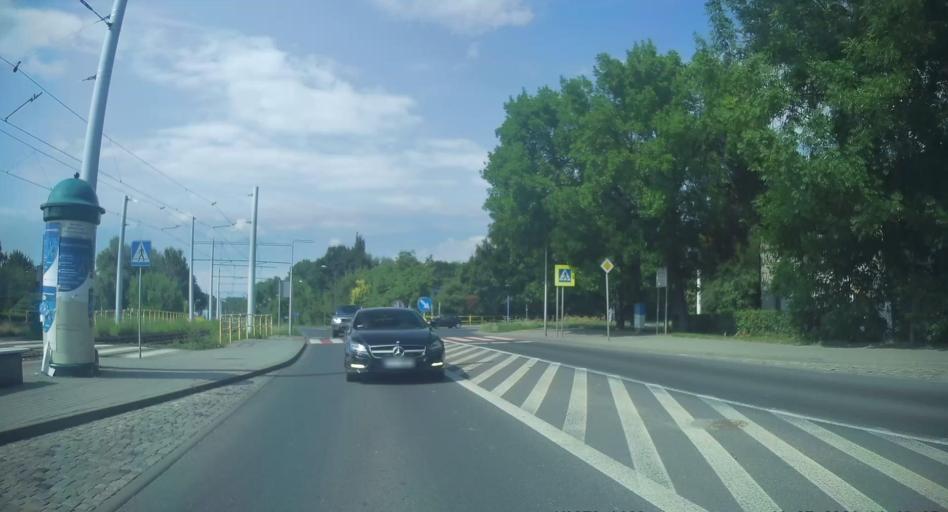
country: PL
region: Silesian Voivodeship
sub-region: Bytom
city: Bytom
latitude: 50.3276
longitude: 18.9281
